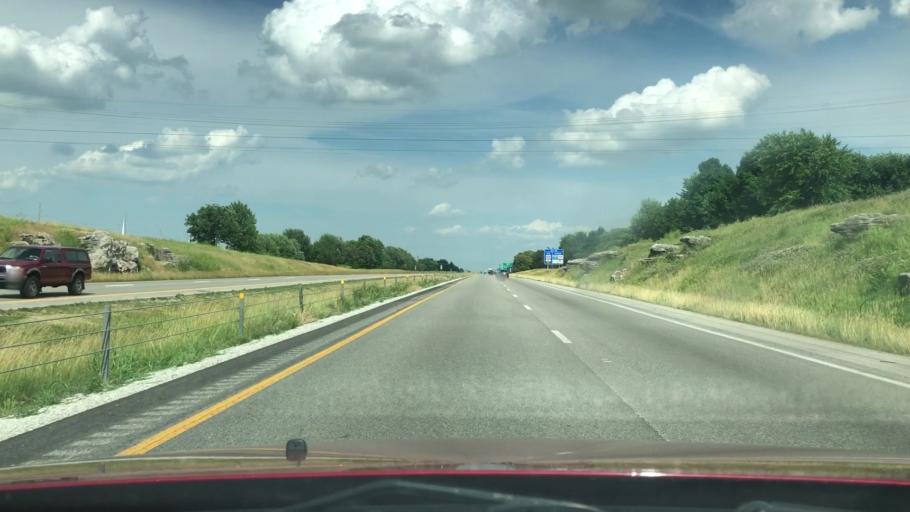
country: US
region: Missouri
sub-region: Greene County
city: Springfield
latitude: 37.2502
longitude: -93.2842
